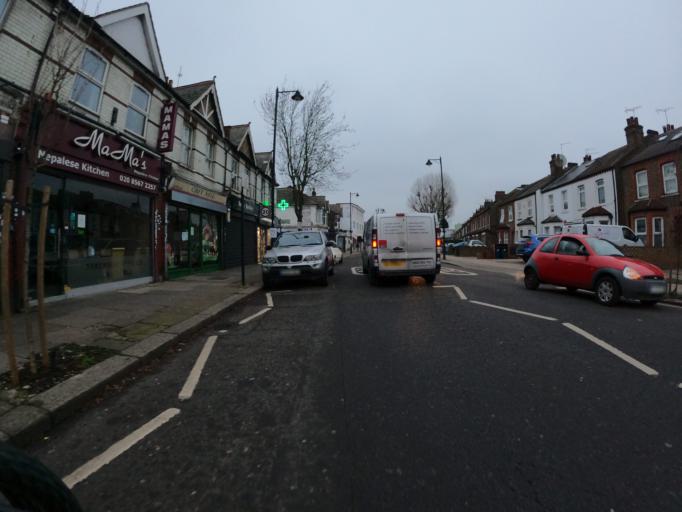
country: GB
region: England
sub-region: Greater London
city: Ealing
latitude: 51.5046
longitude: -0.3189
